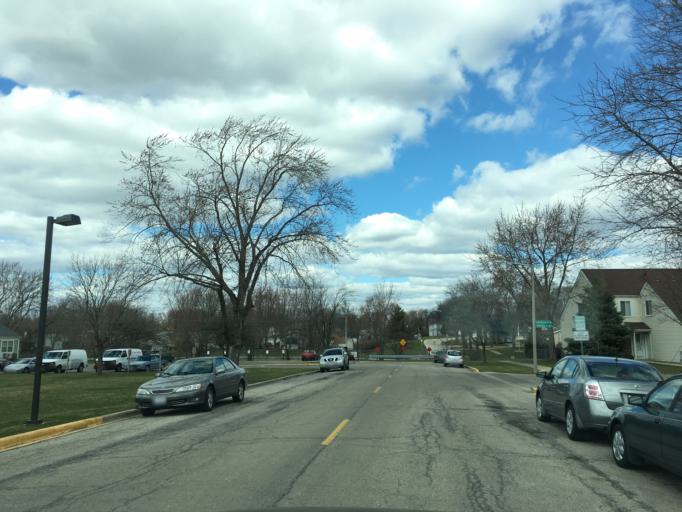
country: US
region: Illinois
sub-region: DuPage County
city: Hanover Park
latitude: 42.0099
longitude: -88.1290
